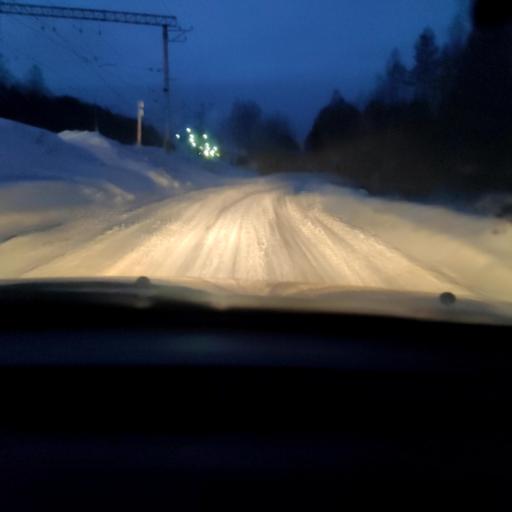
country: RU
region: Perm
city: Kondratovo
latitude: 58.0538
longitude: 55.9985
